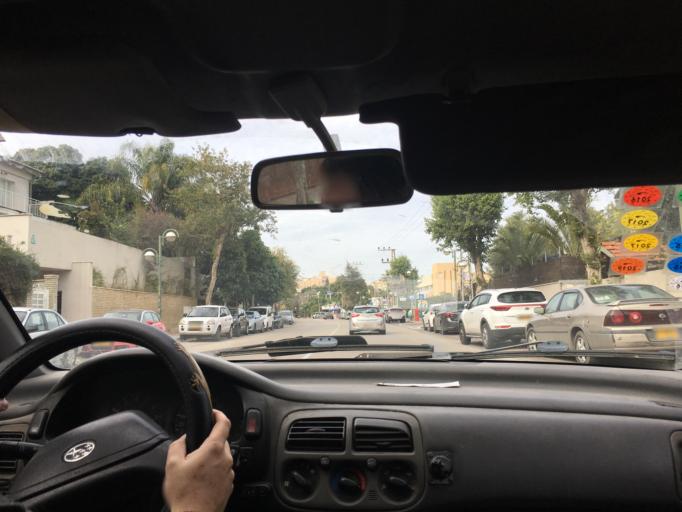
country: IL
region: Tel Aviv
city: Ramat HaSharon
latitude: 32.1358
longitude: 34.8452
